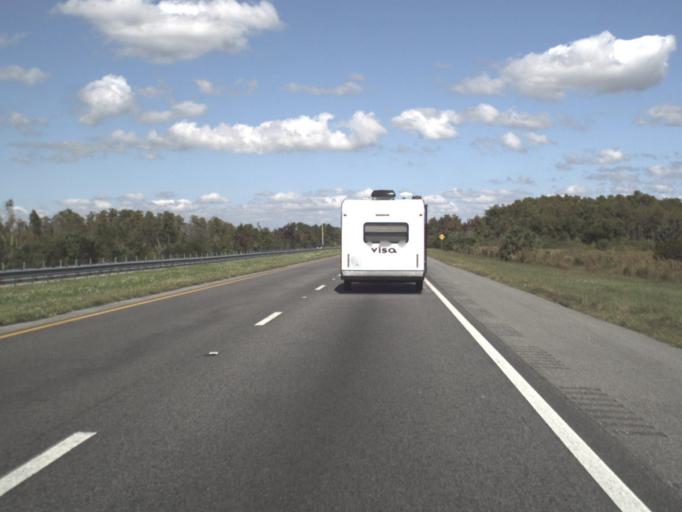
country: US
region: Florida
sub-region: Osceola County
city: Saint Cloud
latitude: 28.1151
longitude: -81.2833
